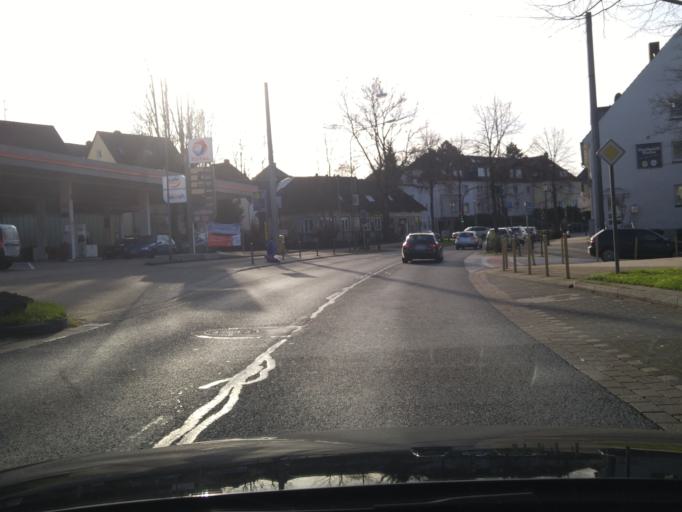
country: DE
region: North Rhine-Westphalia
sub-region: Regierungsbezirk Dusseldorf
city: Essen
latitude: 51.4227
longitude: 7.0286
